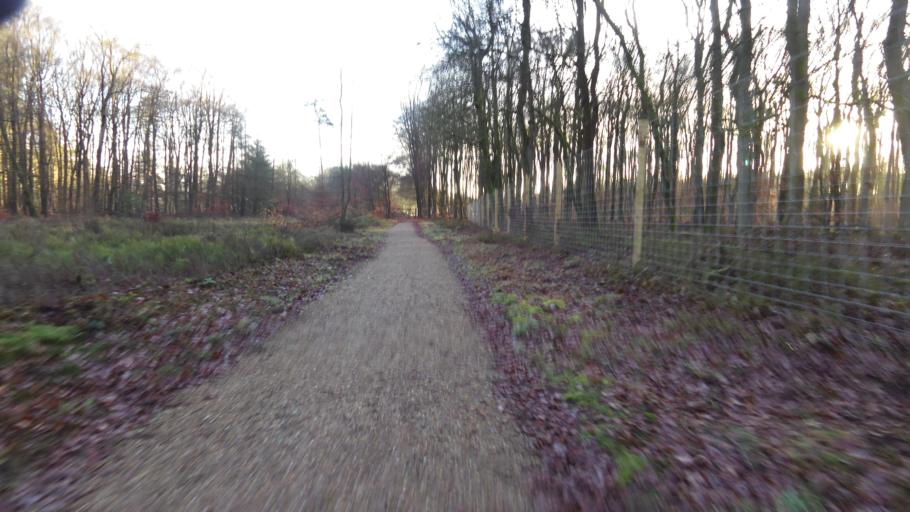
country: NL
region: Gelderland
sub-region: Gemeente Apeldoorn
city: Uddel
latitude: 52.2243
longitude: 5.8659
